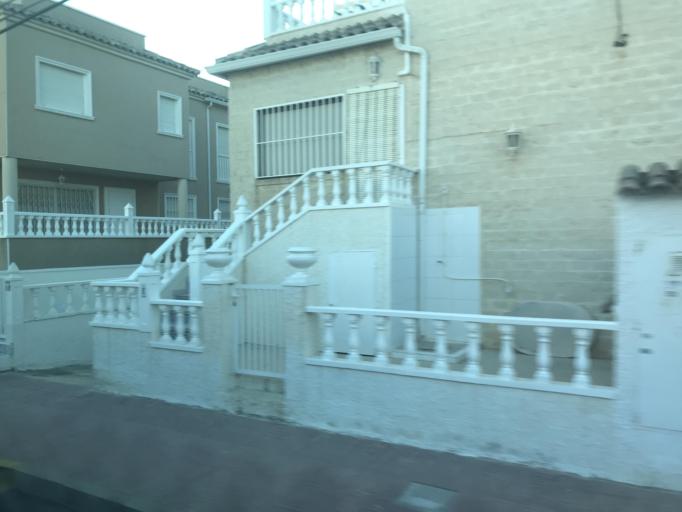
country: ES
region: Valencia
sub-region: Provincia de Alicante
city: Torrevieja
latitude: 38.0219
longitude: -0.6550
